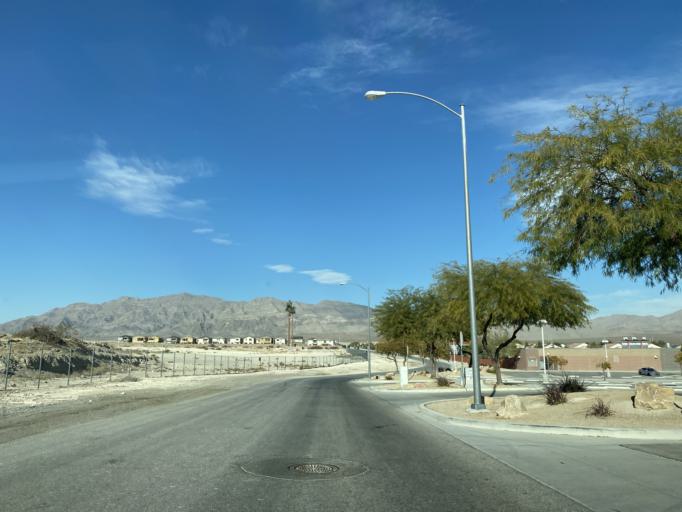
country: US
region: Nevada
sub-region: Clark County
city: North Las Vegas
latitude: 36.2847
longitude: -115.1445
